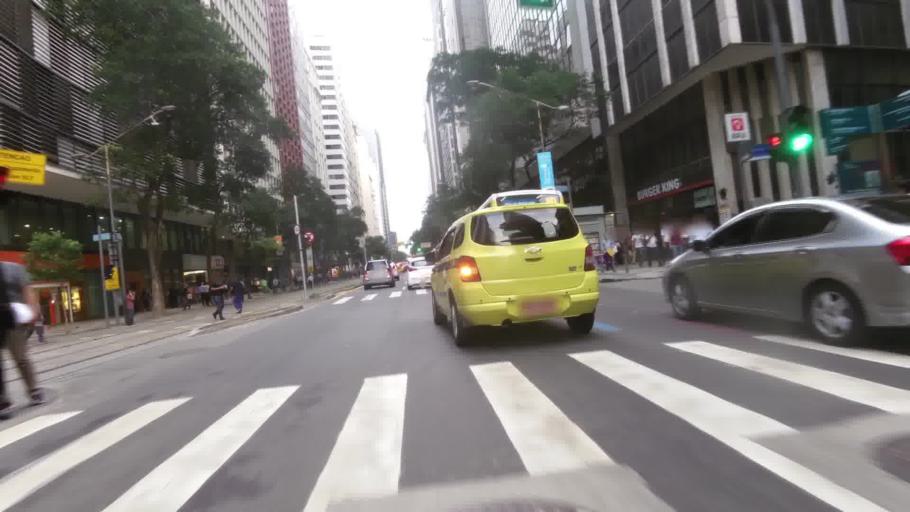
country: BR
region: Rio de Janeiro
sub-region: Rio De Janeiro
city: Rio de Janeiro
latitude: -22.9036
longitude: -43.1782
